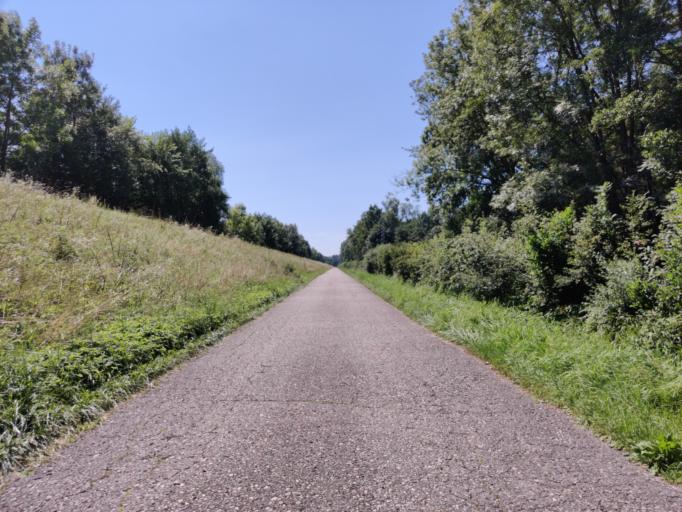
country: AT
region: Styria
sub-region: Politischer Bezirk Leibnitz
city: Gabersdorf
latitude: 46.7952
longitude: 15.5838
